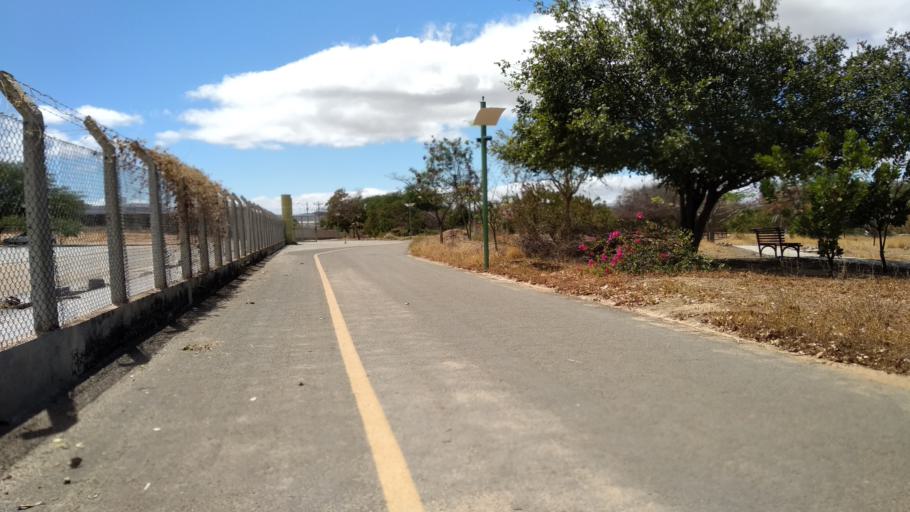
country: BR
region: Bahia
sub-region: Guanambi
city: Guanambi
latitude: -14.2253
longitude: -42.7660
